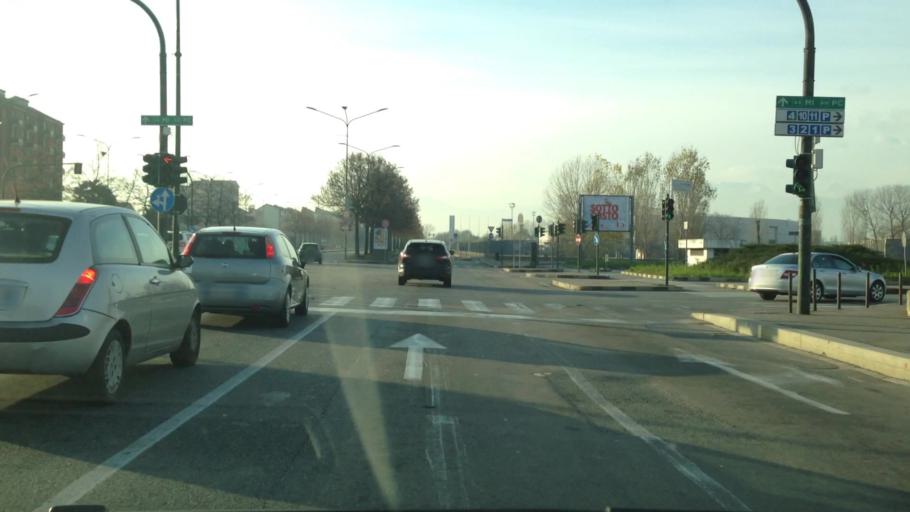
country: IT
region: Piedmont
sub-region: Provincia di Torino
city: Venaria Reale
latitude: 45.1069
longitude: 7.6391
